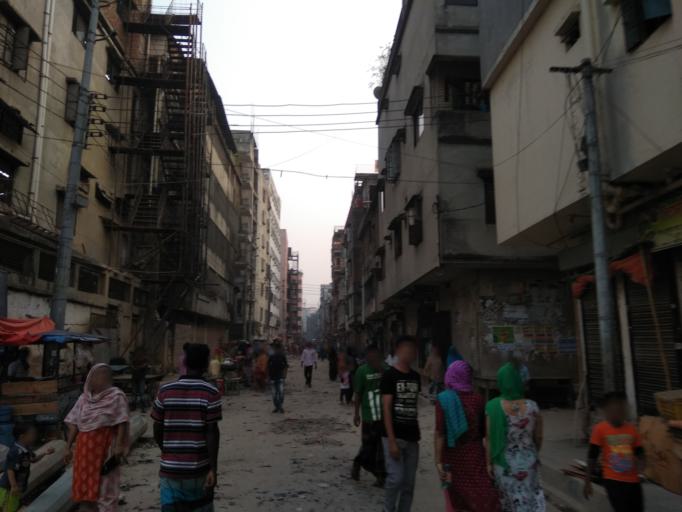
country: BD
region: Dhaka
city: Tungi
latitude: 23.8182
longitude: 90.3638
